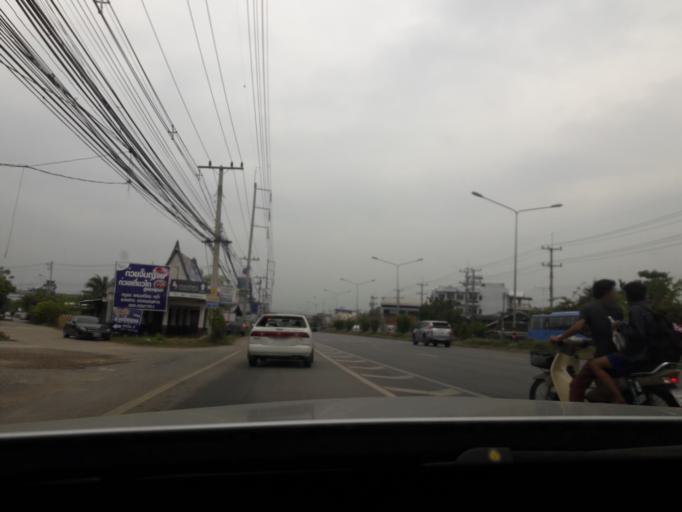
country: TH
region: Samut Songkhram
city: Samut Songkhram
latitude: 13.4173
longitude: 99.9950
